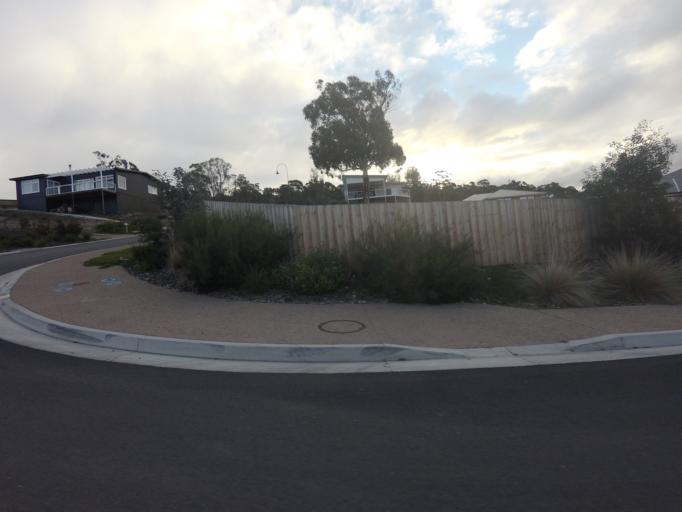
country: AU
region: Tasmania
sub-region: Clarence
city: Rokeby
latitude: -42.9085
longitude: 147.4294
